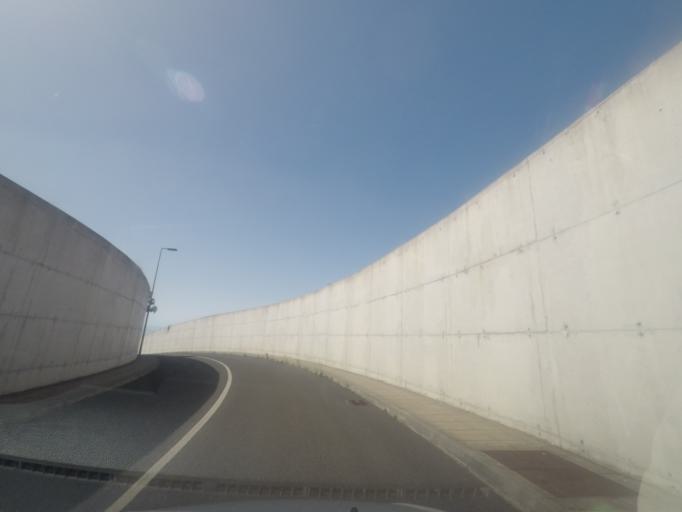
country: PT
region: Madeira
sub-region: Calheta
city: Faja da Ovelha
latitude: 32.8144
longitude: -17.2518
